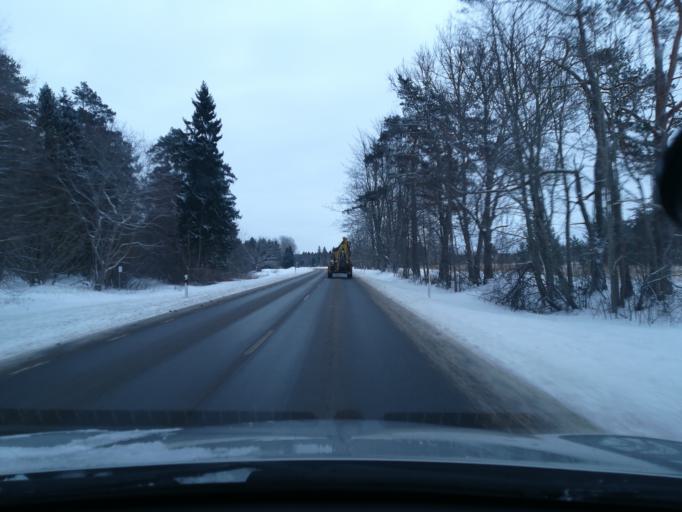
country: EE
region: Harju
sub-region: Keila linn
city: Keila
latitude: 59.3955
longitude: 24.2778
